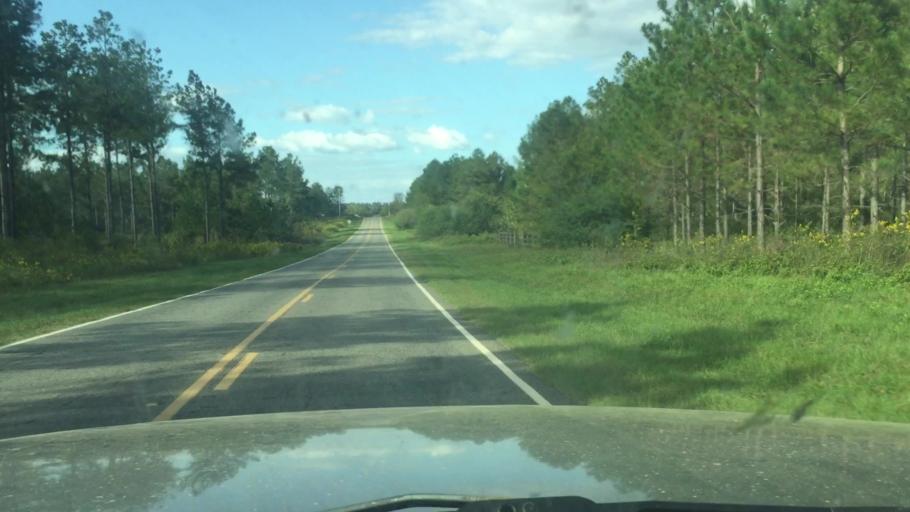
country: US
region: Georgia
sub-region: Terrell County
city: Dawson
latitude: 31.7443
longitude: -84.3506
